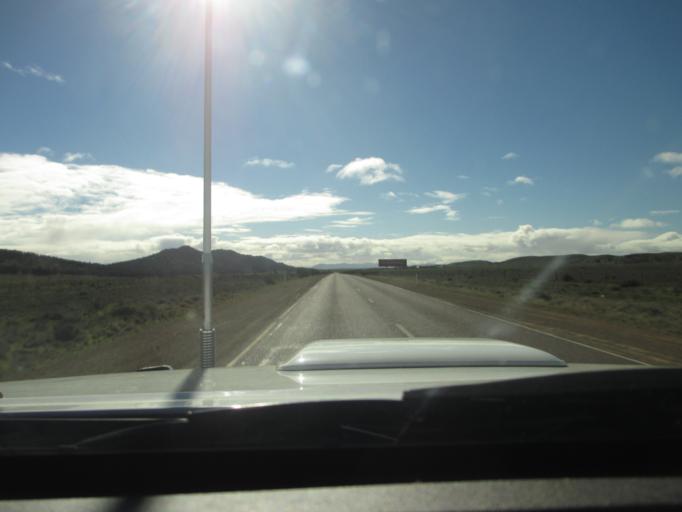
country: AU
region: South Australia
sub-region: Flinders Ranges
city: Quorn
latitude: -31.9488
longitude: 138.3971
